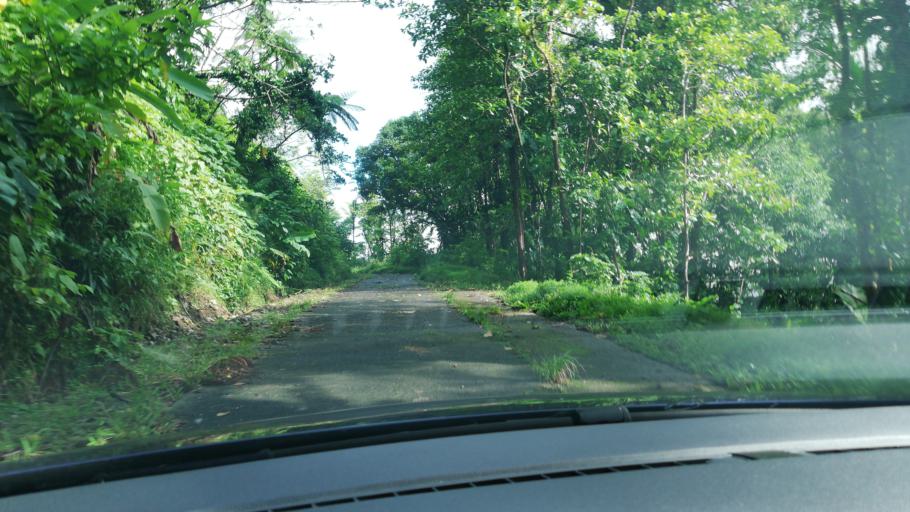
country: GP
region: Guadeloupe
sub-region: Guadeloupe
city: Bouillante
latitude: 16.1854
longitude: -61.7476
